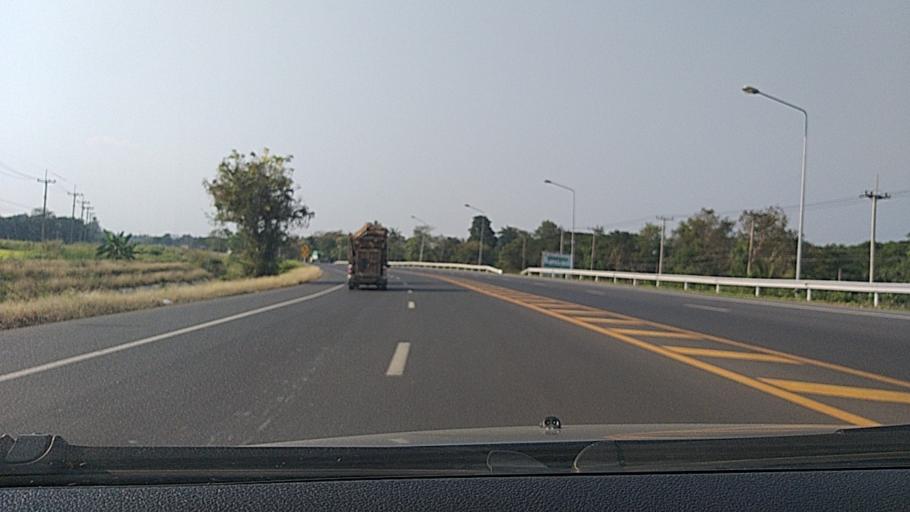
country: TH
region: Sing Buri
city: Phrom Buri
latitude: 14.7961
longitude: 100.4435
